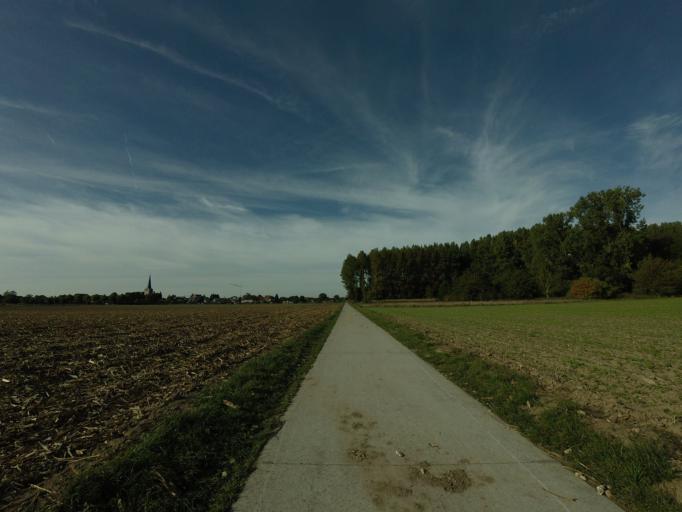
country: BE
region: Flanders
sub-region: Provincie Vlaams-Brabant
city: Kampenhout
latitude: 50.9168
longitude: 4.5710
